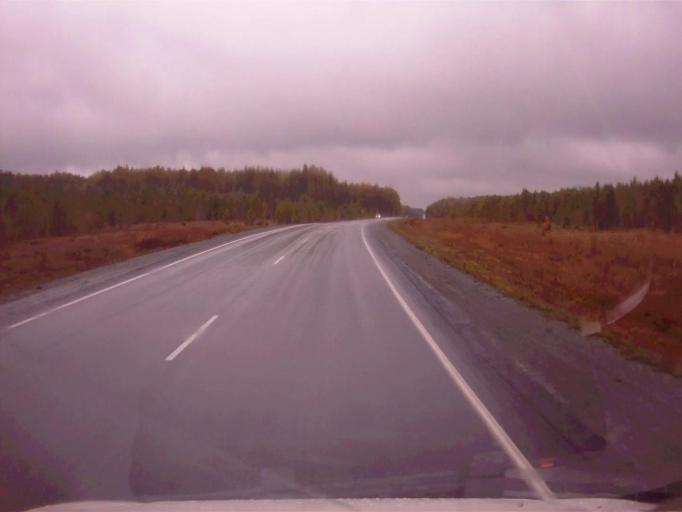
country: RU
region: Chelyabinsk
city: Tayginka
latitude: 55.5064
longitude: 60.6368
